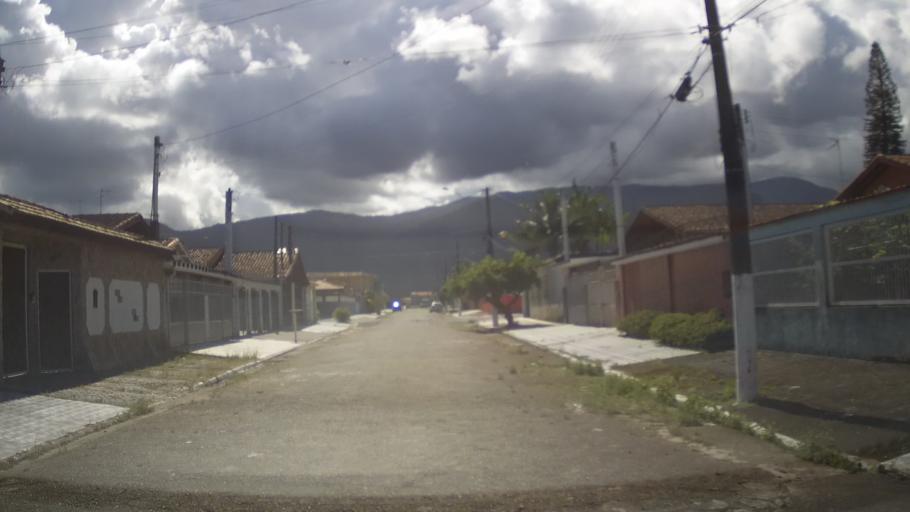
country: BR
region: Sao Paulo
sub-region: Mongagua
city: Mongagua
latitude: -24.0643
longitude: -46.5612
